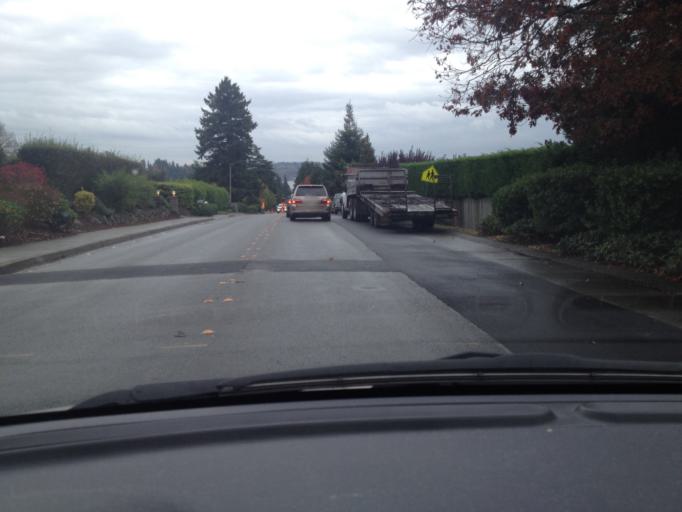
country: US
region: Washington
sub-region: King County
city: Clyde Hill
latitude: 47.6238
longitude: -122.2179
